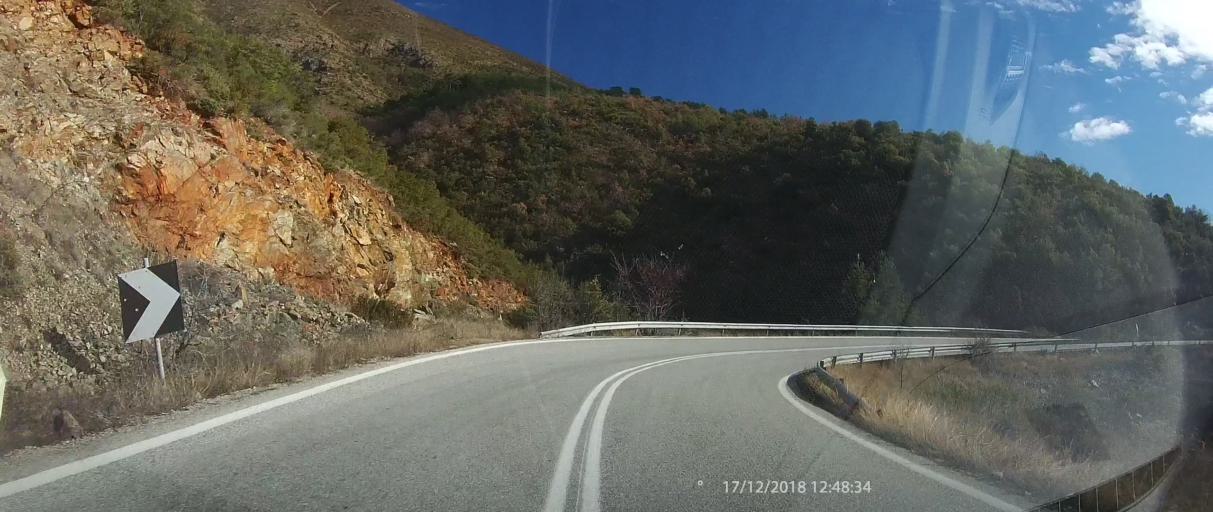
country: GR
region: Thessaly
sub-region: Trikala
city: Kastraki
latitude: 39.7845
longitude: 21.4377
